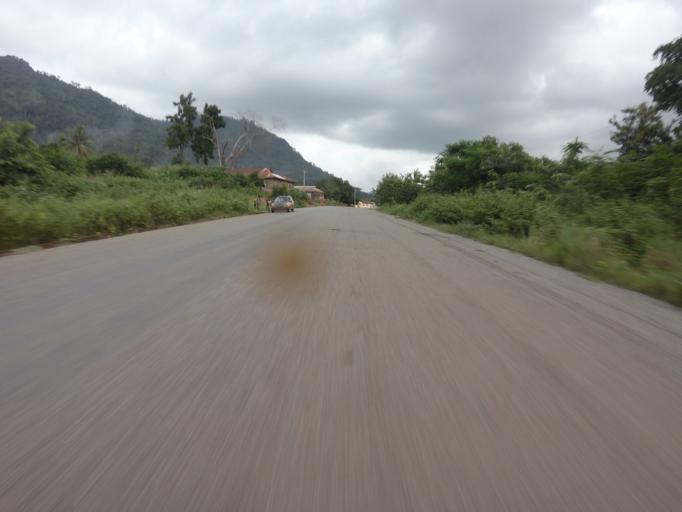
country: GH
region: Volta
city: Kpandu
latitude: 6.8011
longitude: 0.3729
